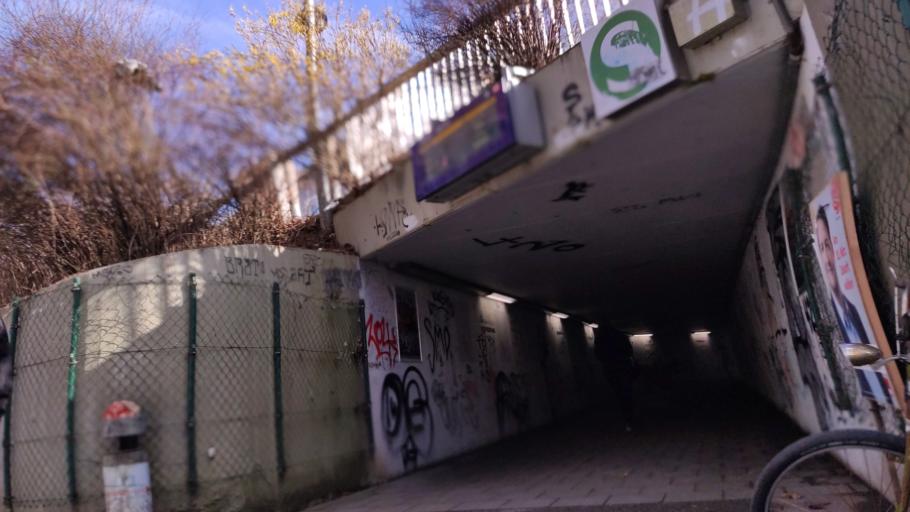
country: DE
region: Bavaria
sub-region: Upper Bavaria
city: Fuerstenfeldbruck
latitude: 48.1723
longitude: 11.2616
